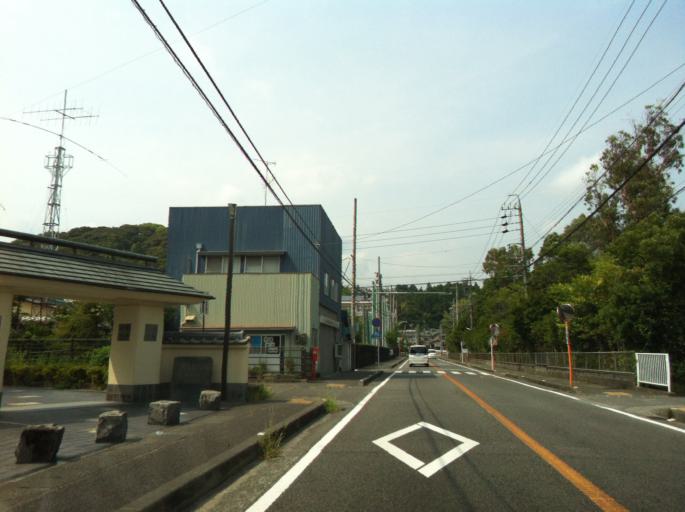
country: JP
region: Shizuoka
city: Shimada
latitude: 34.8424
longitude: 138.1753
